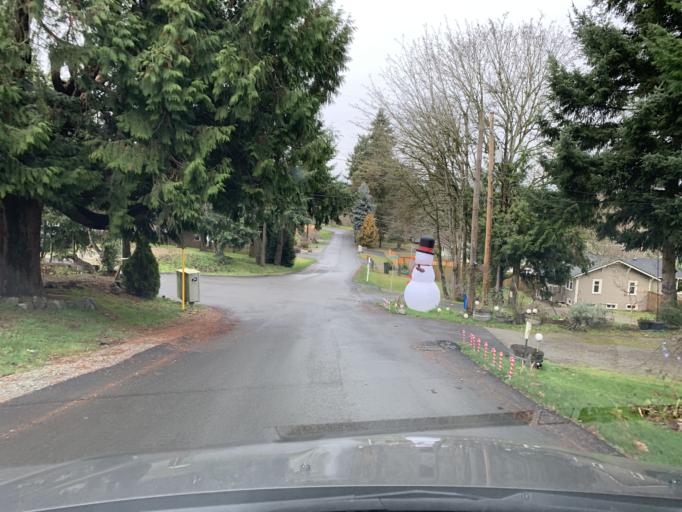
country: US
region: Washington
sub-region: King County
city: Tukwila
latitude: 47.4616
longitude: -122.2752
